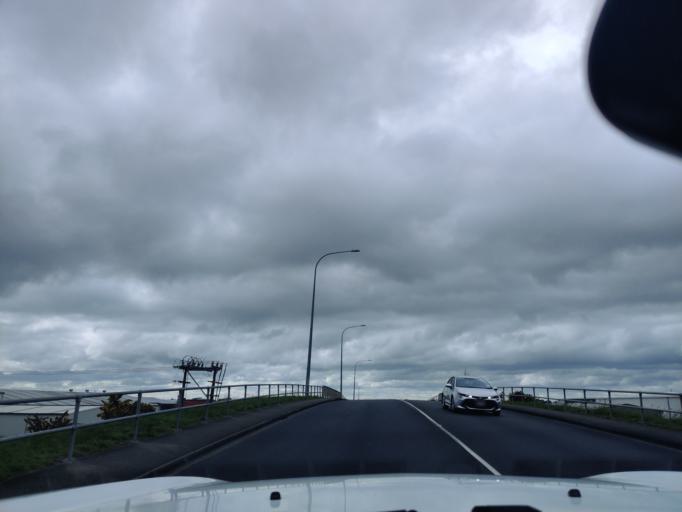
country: NZ
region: Manawatu-Wanganui
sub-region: Palmerston North City
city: Palmerston North
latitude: -40.3380
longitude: 175.6437
